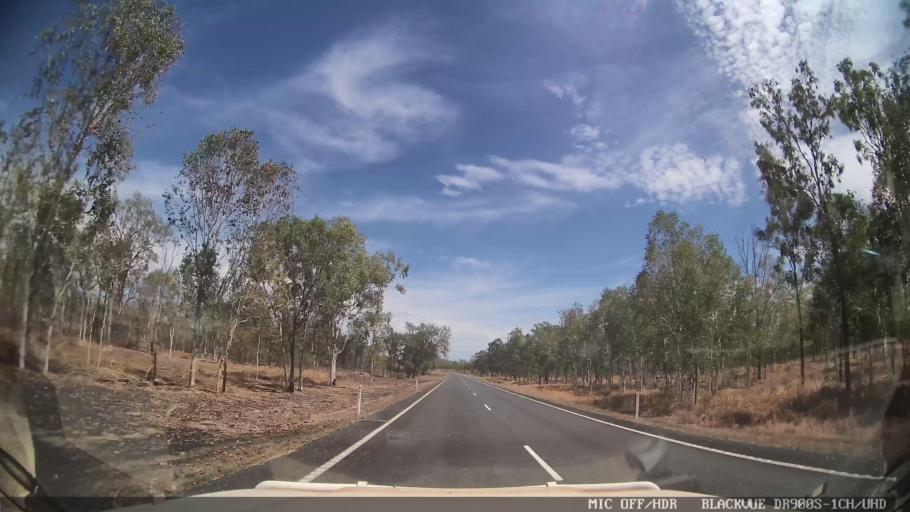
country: AU
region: Queensland
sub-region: Cook
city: Cooktown
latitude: -15.7578
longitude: 145.0034
